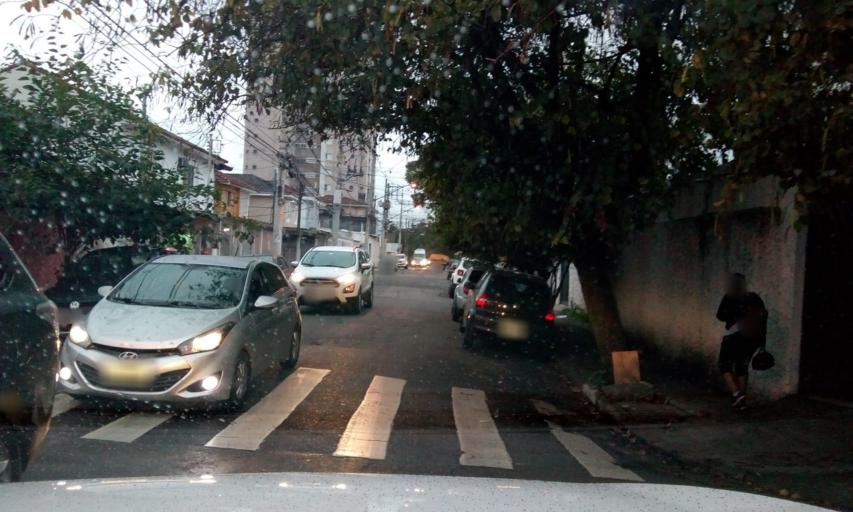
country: BR
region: Sao Paulo
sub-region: Sao Paulo
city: Sao Paulo
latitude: -23.6091
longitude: -46.6899
